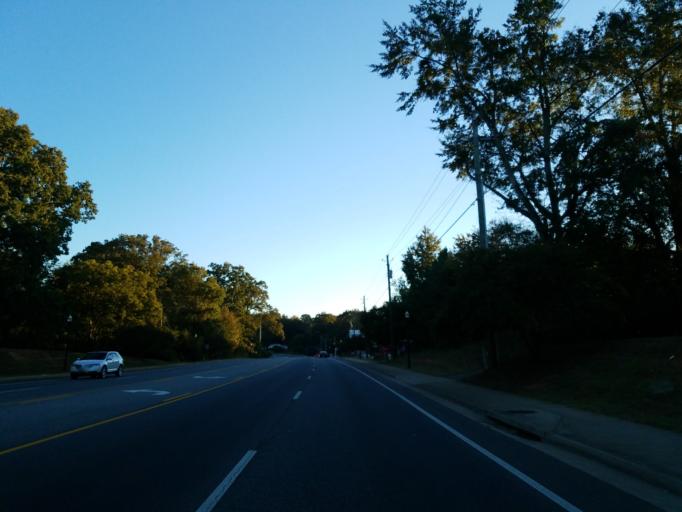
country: US
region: Georgia
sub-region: Forsyth County
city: Cumming
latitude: 34.1998
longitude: -84.1404
